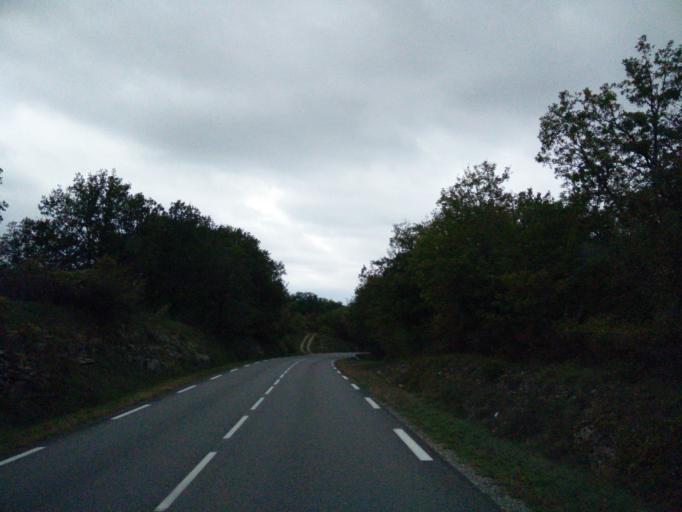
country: FR
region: Midi-Pyrenees
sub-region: Departement du Lot
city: Luzech
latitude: 44.5259
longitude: 1.3241
